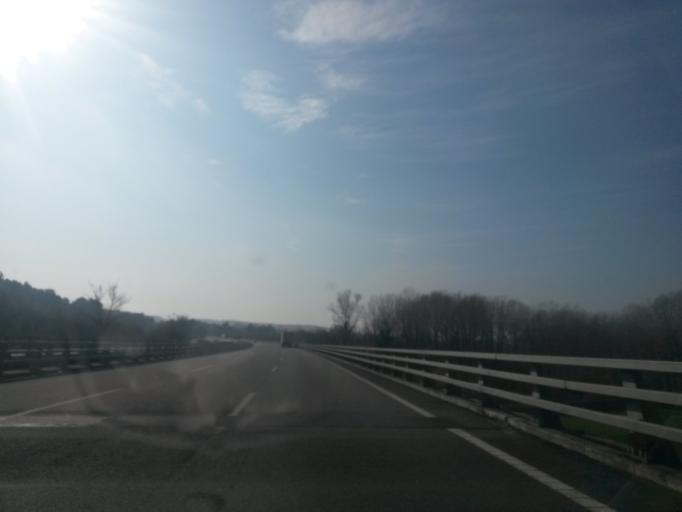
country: ES
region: Catalonia
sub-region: Provincia de Girona
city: Bascara
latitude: 42.1643
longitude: 2.9207
